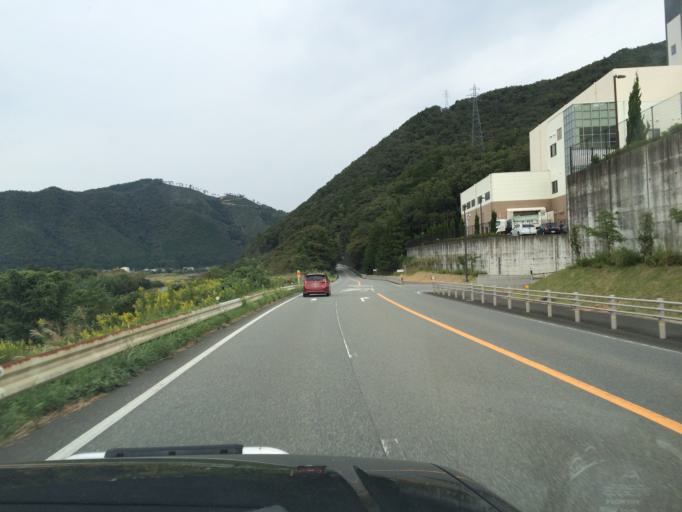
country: JP
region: Hyogo
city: Toyooka
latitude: 35.3660
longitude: 134.8238
